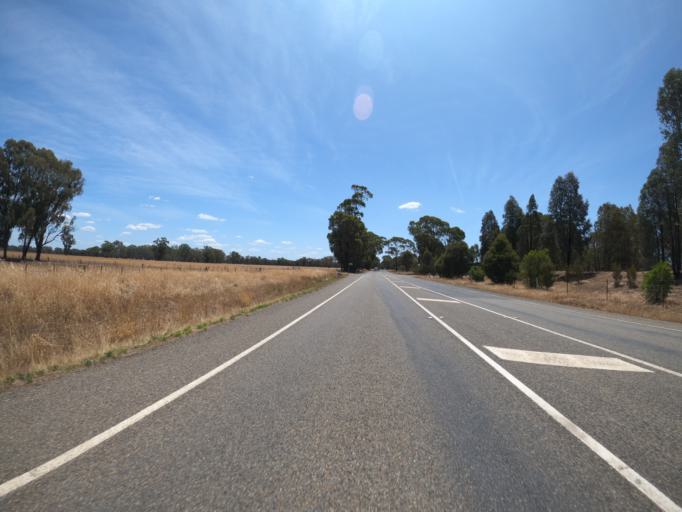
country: AU
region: Victoria
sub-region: Benalla
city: Benalla
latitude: -36.4964
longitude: 146.0193
